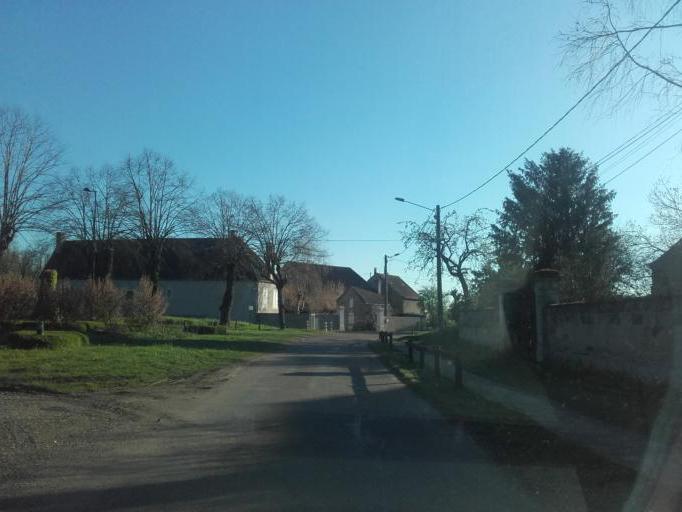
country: FR
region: Bourgogne
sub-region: Departement de Saone-et-Loire
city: Demigny
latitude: 46.9408
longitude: 4.8202
